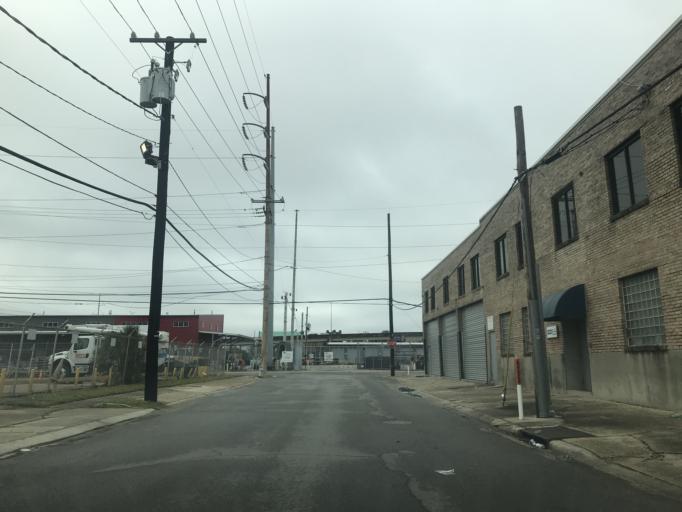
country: US
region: Louisiana
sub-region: Orleans Parish
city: New Orleans
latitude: 29.9665
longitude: -90.1030
